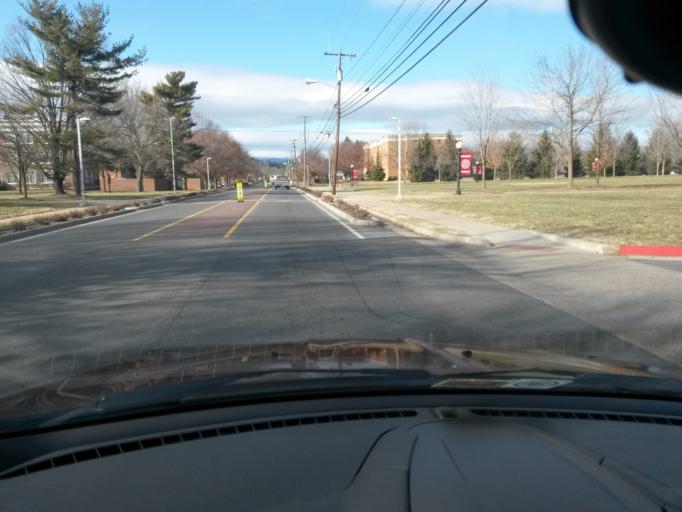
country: US
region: Virginia
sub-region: Rockingham County
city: Bridgewater
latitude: 38.3795
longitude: -78.9684
